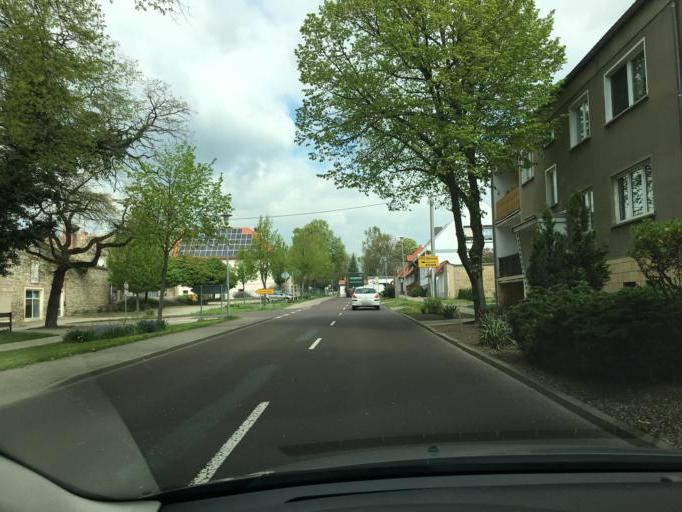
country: DE
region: Saxony-Anhalt
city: Giersleben
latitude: 51.7378
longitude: 11.5915
